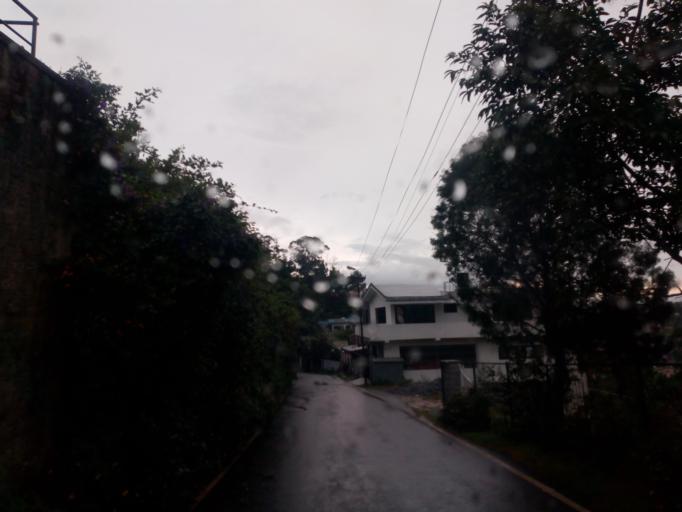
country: IN
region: Tamil Nadu
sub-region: Nilgiri
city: Wellington
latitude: 11.3508
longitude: 76.8086
